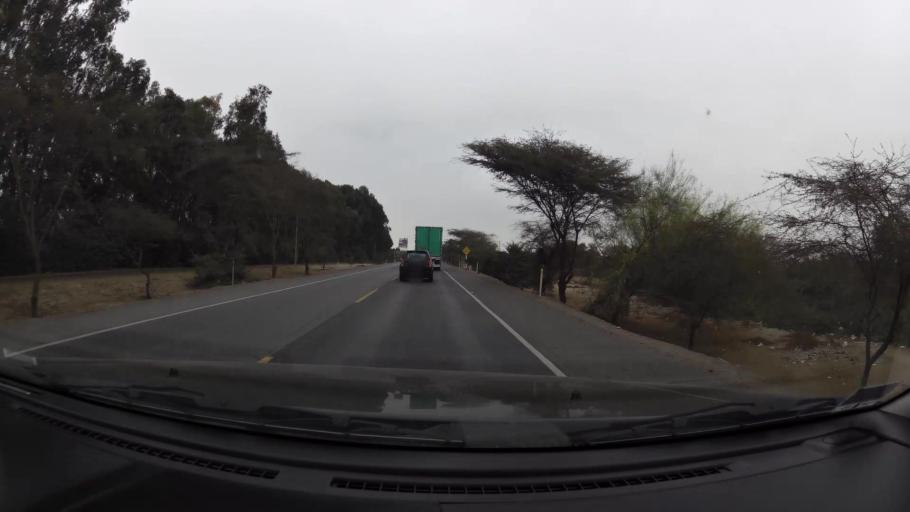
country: PE
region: Ica
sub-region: Provincia de Pisco
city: Villa Tupac Amaru
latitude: -13.8255
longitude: -76.1424
